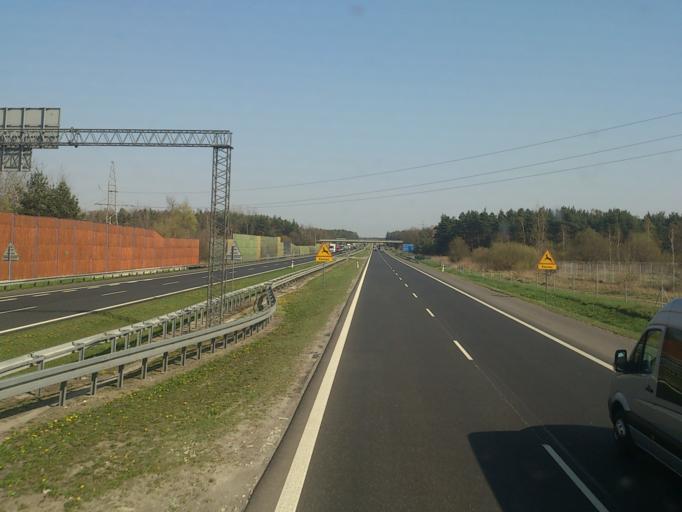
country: PL
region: Lesser Poland Voivodeship
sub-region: Powiat chrzanowski
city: Trzebinia
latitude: 50.1452
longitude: 19.4381
